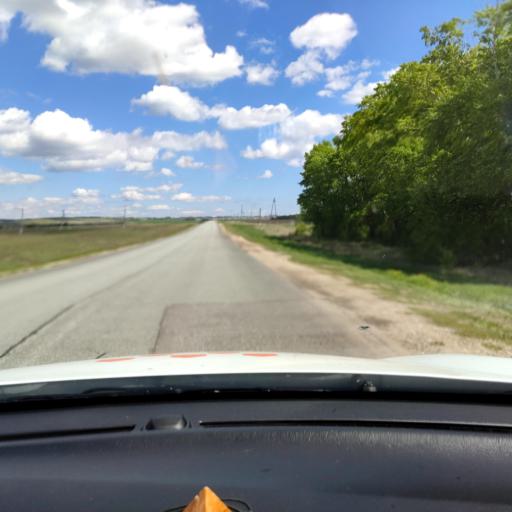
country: RU
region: Tatarstan
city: Kuybyshevskiy Zaton
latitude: 55.1622
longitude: 49.1981
